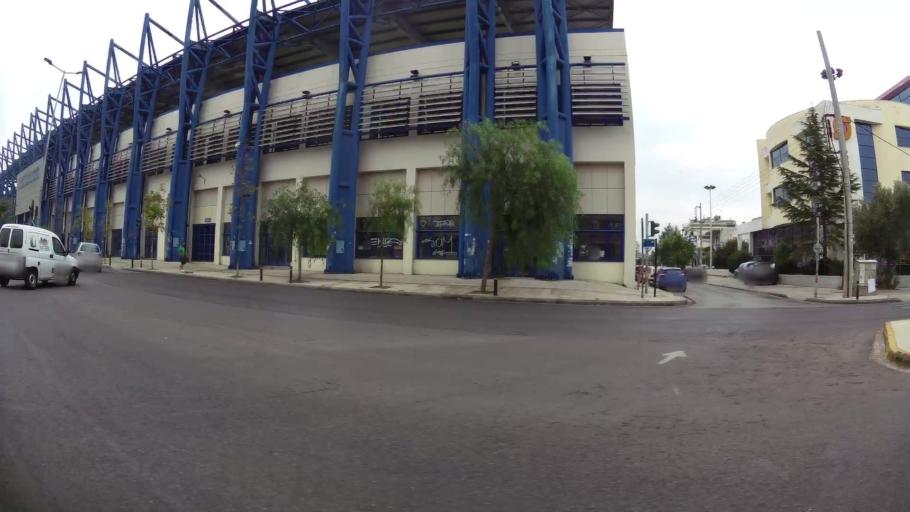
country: GR
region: Attica
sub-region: Nomarchia Athinas
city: Aigaleo
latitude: 37.9871
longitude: 23.6748
